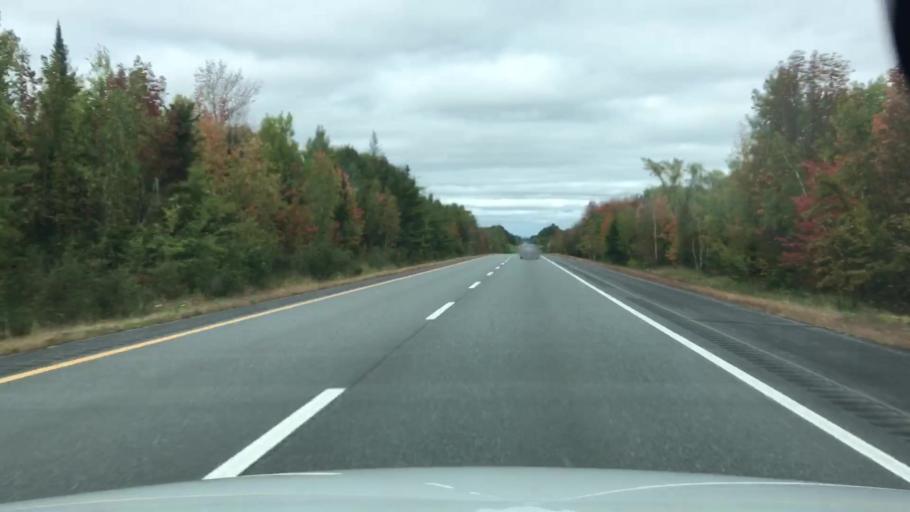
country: US
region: Maine
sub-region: Waldo County
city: Burnham
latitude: 44.7362
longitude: -69.4318
